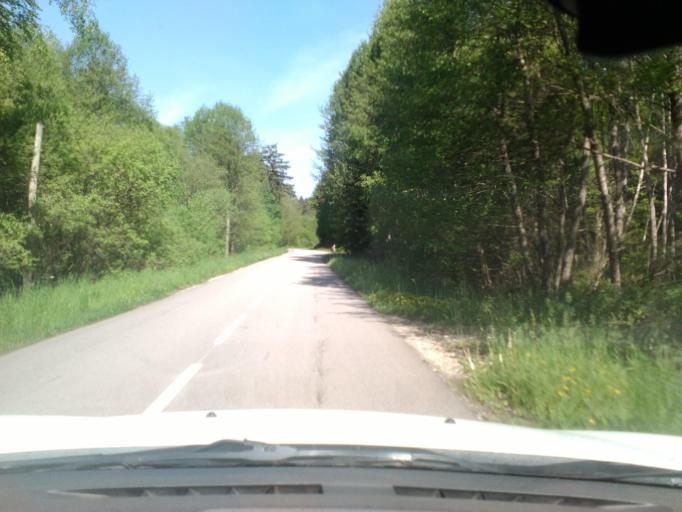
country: FR
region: Lorraine
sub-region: Departement des Vosges
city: Bruyeres
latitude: 48.2673
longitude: 6.7255
